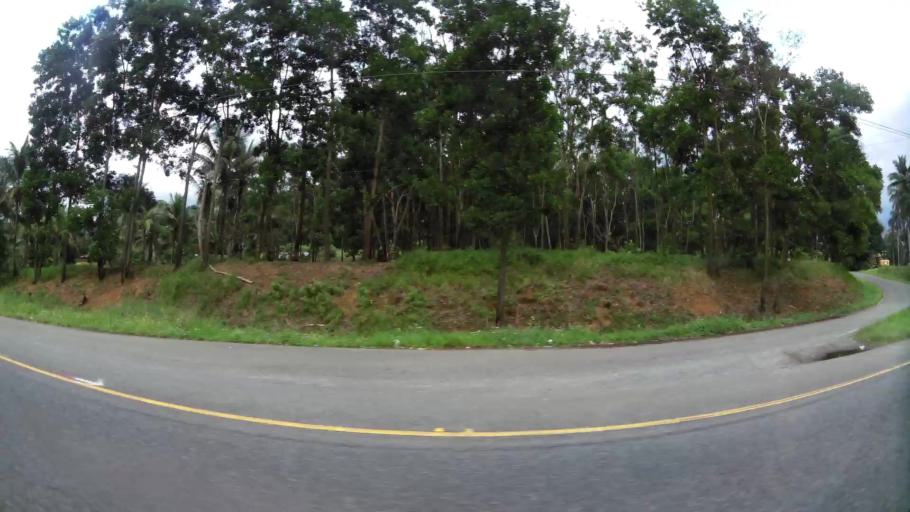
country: DO
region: Monsenor Nouel
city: Piedra Blanca
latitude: 18.7938
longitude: -70.2716
